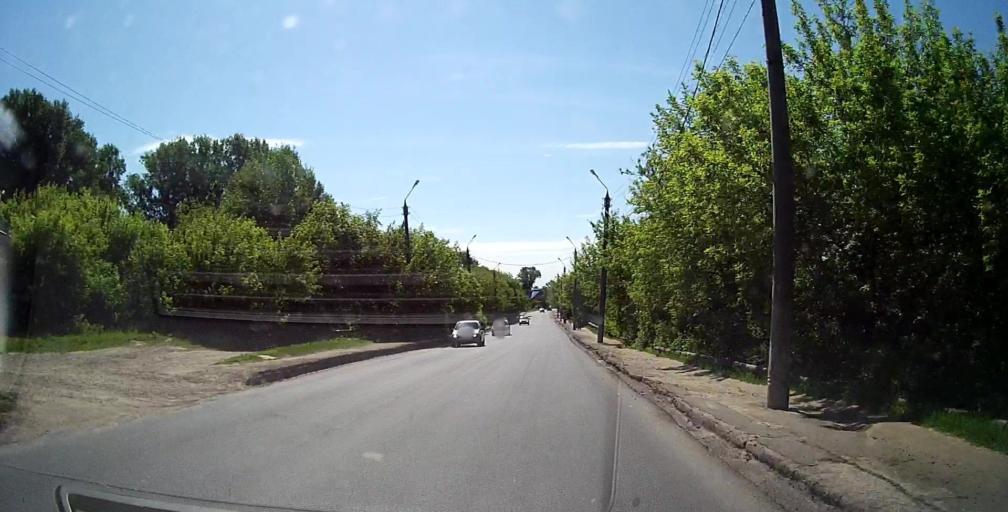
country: RU
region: Lipetsk
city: Dankov
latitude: 53.2430
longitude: 39.1431
